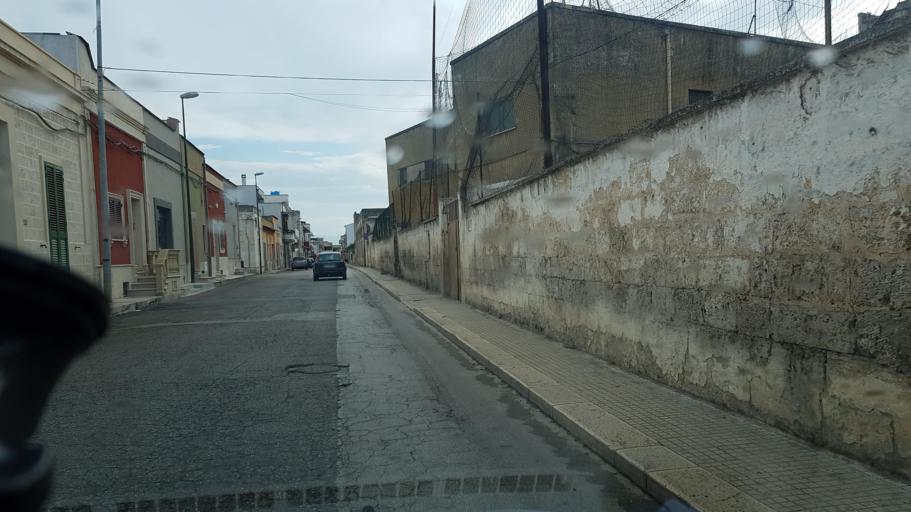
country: IT
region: Apulia
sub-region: Provincia di Brindisi
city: Torre Santa Susanna
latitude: 40.4636
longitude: 17.7447
